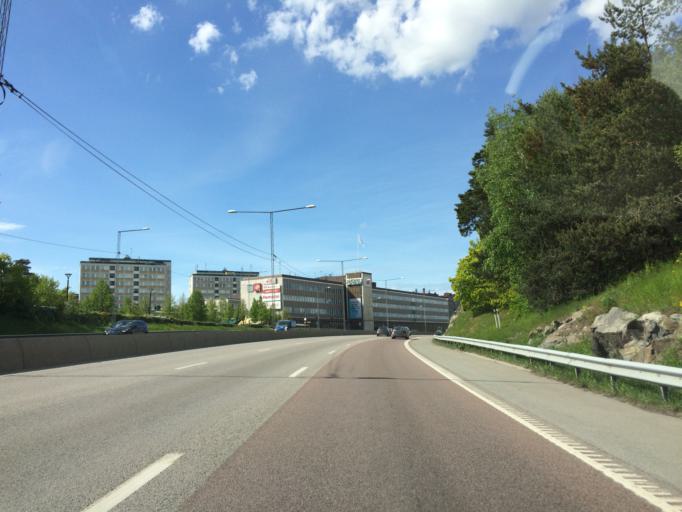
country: SE
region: Stockholm
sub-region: Norrtalje Kommun
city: Bergshamra
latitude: 59.3959
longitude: 18.0393
